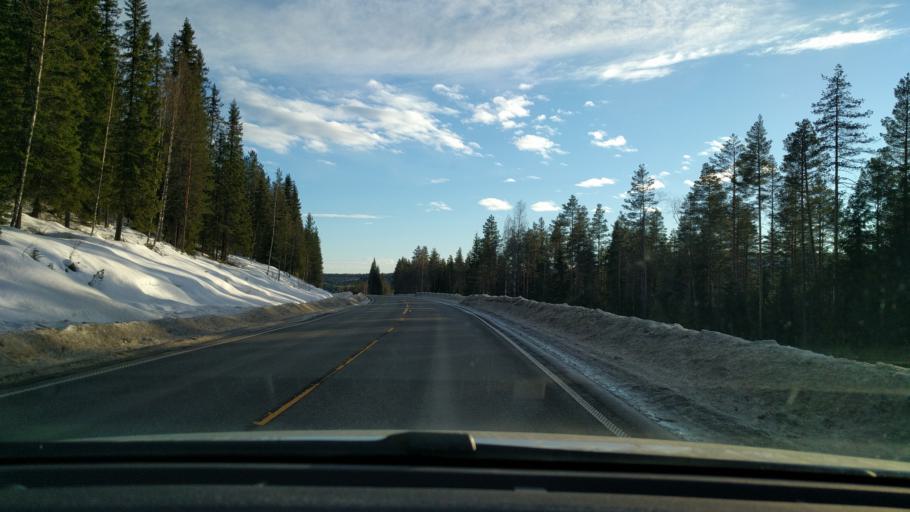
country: NO
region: Hedmark
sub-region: Elverum
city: Elverum
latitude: 61.0437
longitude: 11.8743
